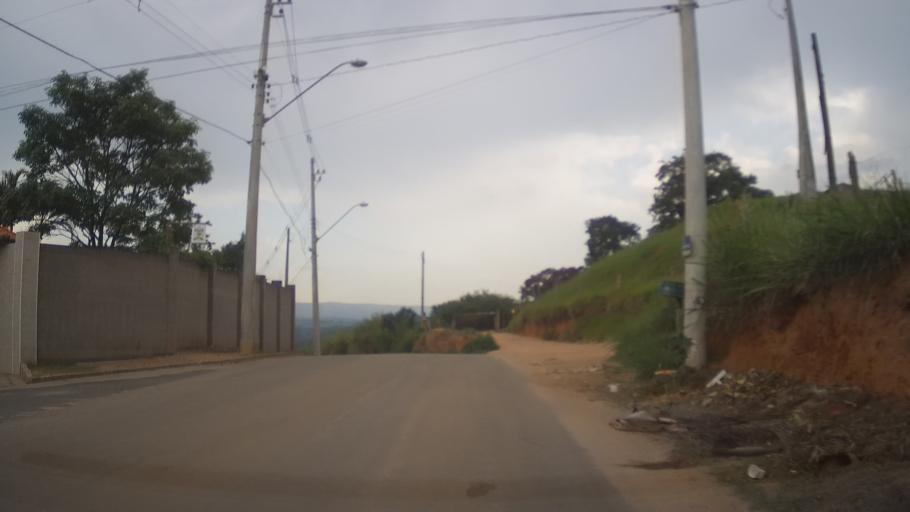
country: BR
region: Sao Paulo
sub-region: Itupeva
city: Itupeva
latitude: -23.1800
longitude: -47.0897
